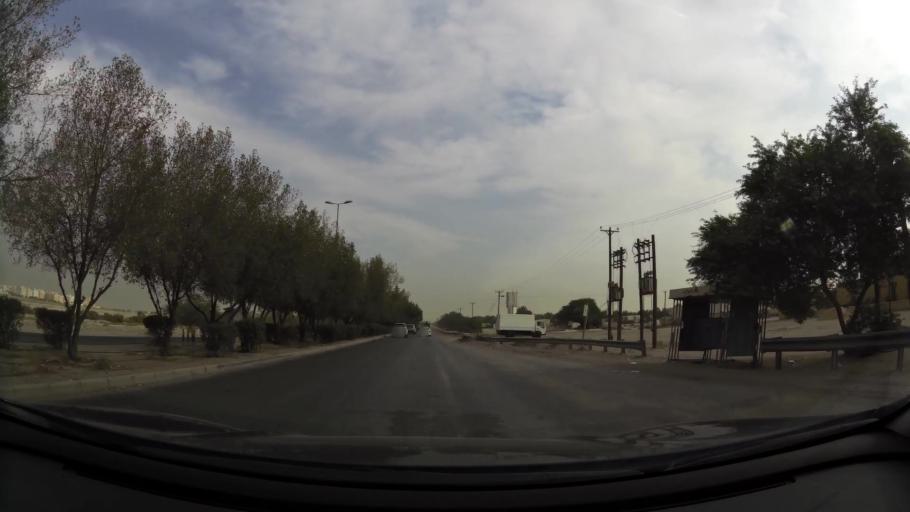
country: KW
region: Muhafazat al Jahra'
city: Al Jahra'
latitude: 29.3166
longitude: 47.7470
